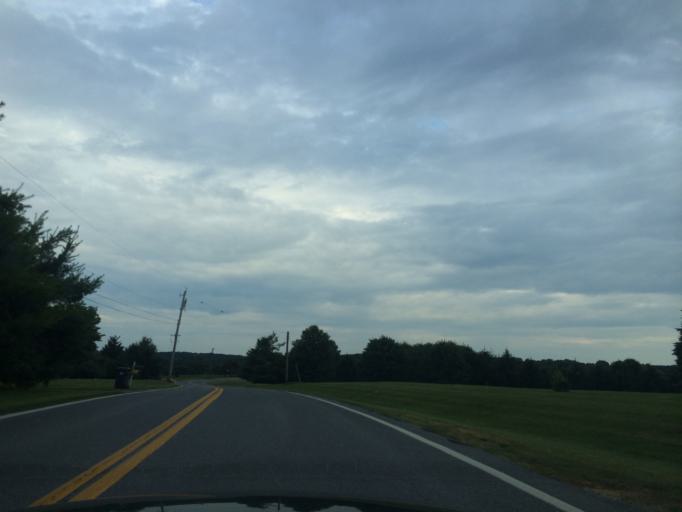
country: US
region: Maryland
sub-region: Carroll County
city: Sykesville
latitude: 39.4013
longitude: -77.0054
